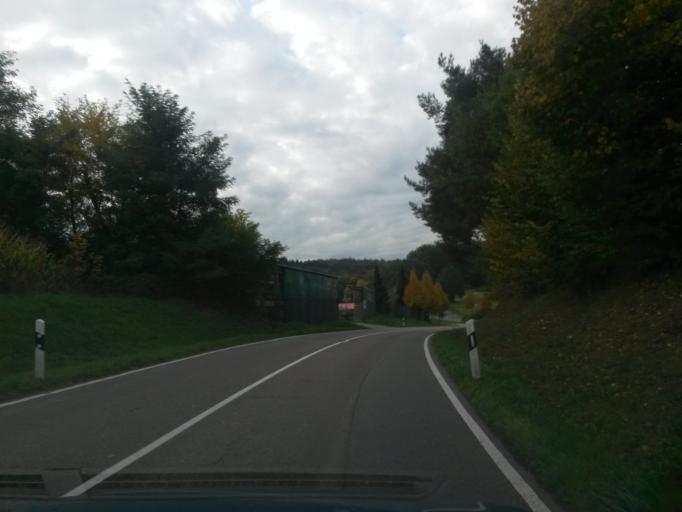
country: DE
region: Baden-Wuerttemberg
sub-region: Karlsruhe Region
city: Neuenburg
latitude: 48.8943
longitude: 8.5765
